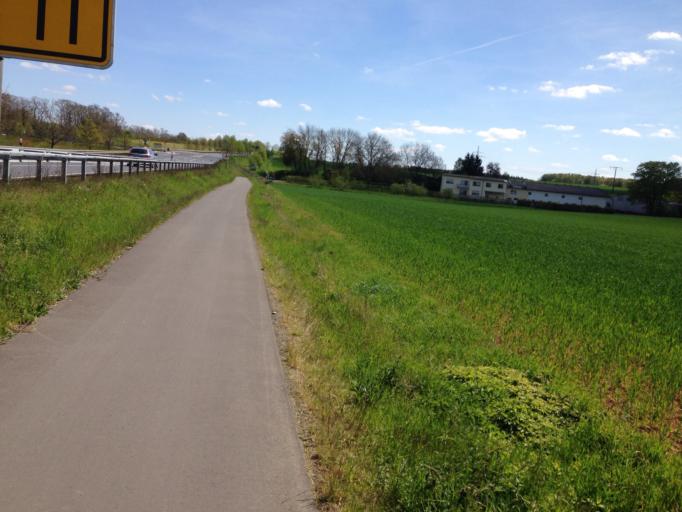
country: DE
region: Hesse
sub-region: Regierungsbezirk Giessen
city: Hungen
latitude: 50.4789
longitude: 8.8745
